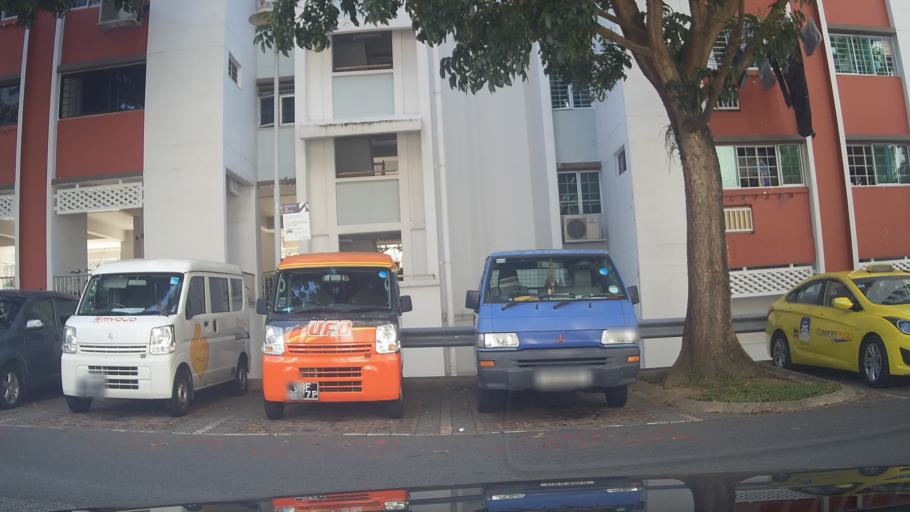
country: MY
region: Johor
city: Johor Bahru
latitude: 1.4382
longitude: 103.7775
